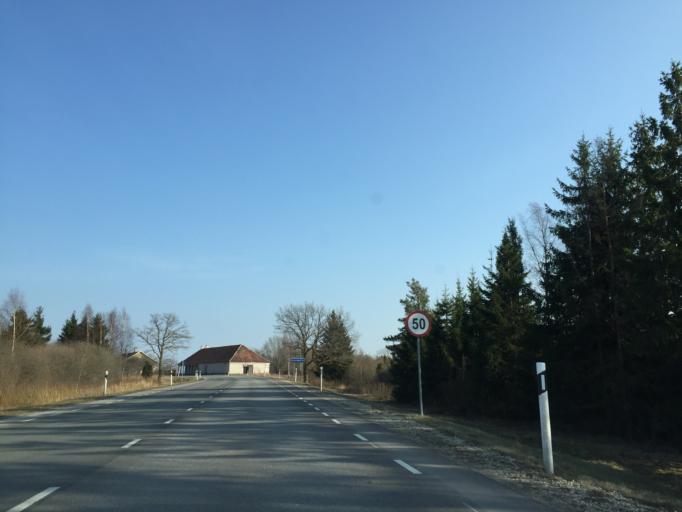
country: EE
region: Saare
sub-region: Orissaare vald
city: Orissaare
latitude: 58.5733
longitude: 23.3787
